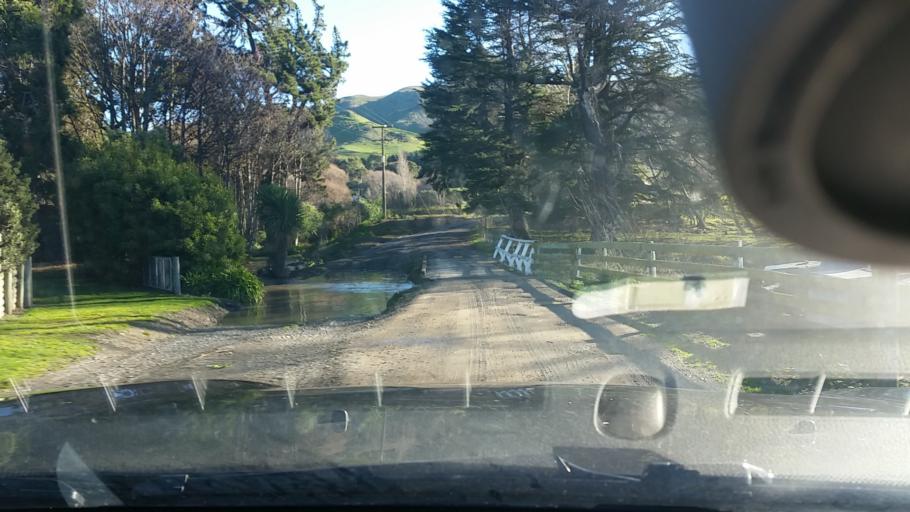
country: NZ
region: Marlborough
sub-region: Marlborough District
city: Blenheim
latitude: -41.6386
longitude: 174.0235
